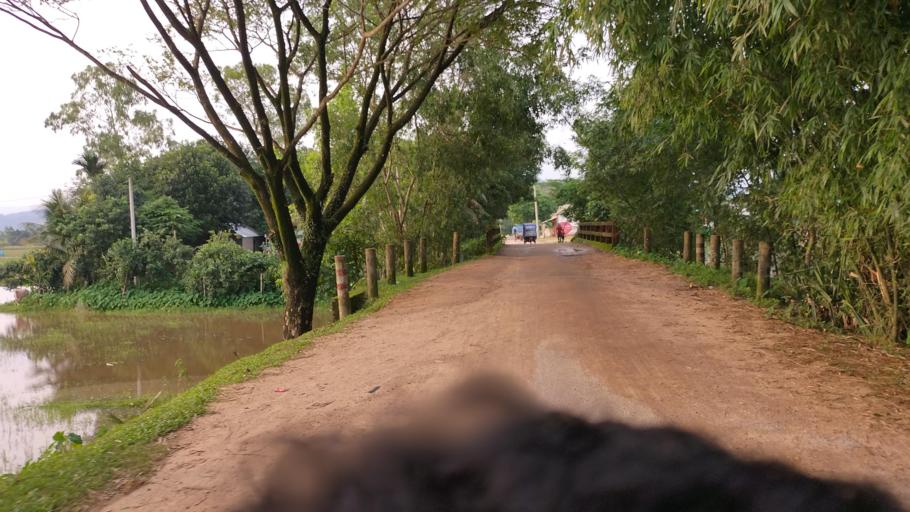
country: BD
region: Dhaka
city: Netrakona
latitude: 25.1332
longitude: 90.9135
